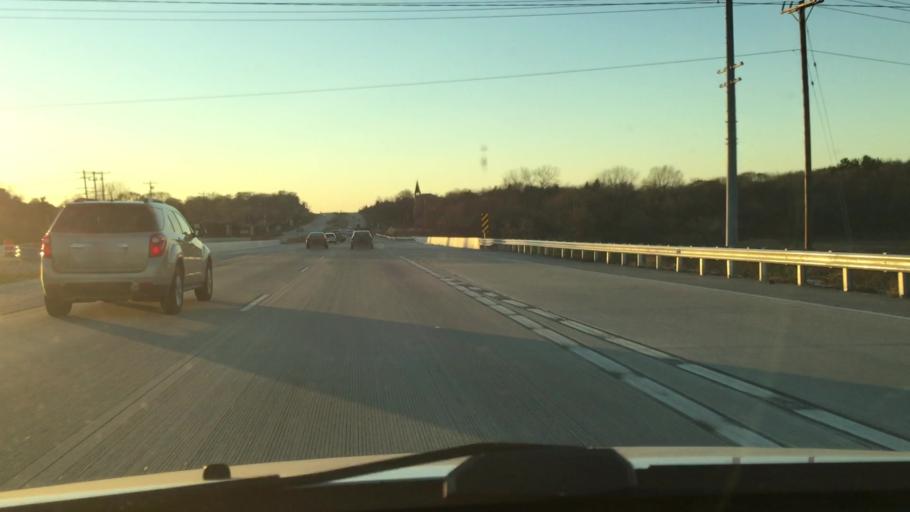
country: US
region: Wisconsin
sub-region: Waukesha County
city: Sussex
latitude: 43.0833
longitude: -88.2044
